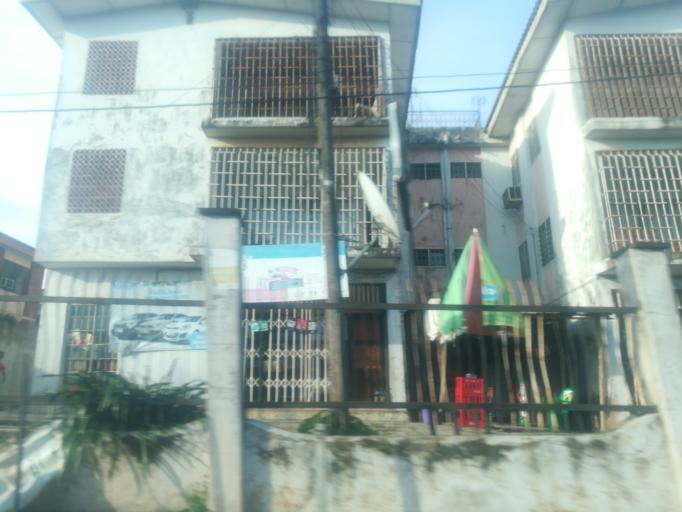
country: NG
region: Oyo
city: Ibadan
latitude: 7.3434
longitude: 3.8880
